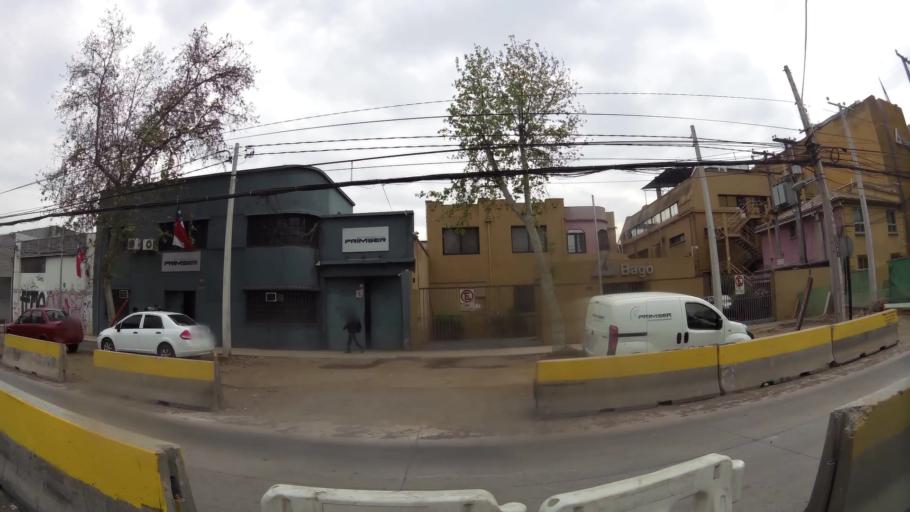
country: CL
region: Santiago Metropolitan
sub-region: Provincia de Santiago
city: Santiago
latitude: -33.4679
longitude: -70.6263
